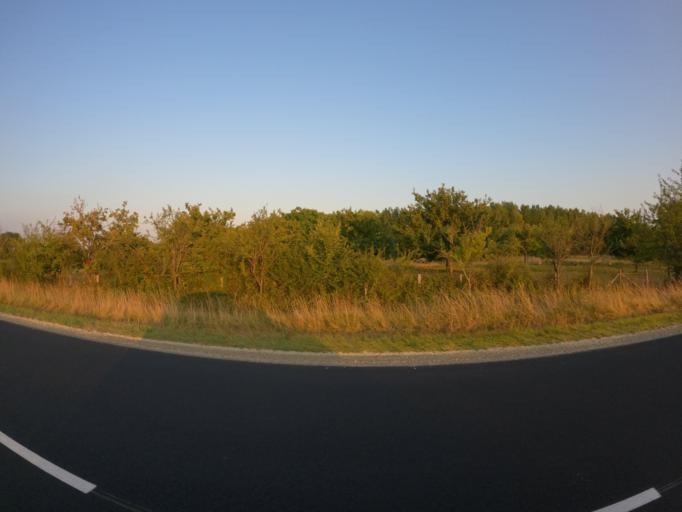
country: FR
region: Pays de la Loire
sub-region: Departement de la Sarthe
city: Auvers-le-Hamon
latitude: 47.8689
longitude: -0.4077
